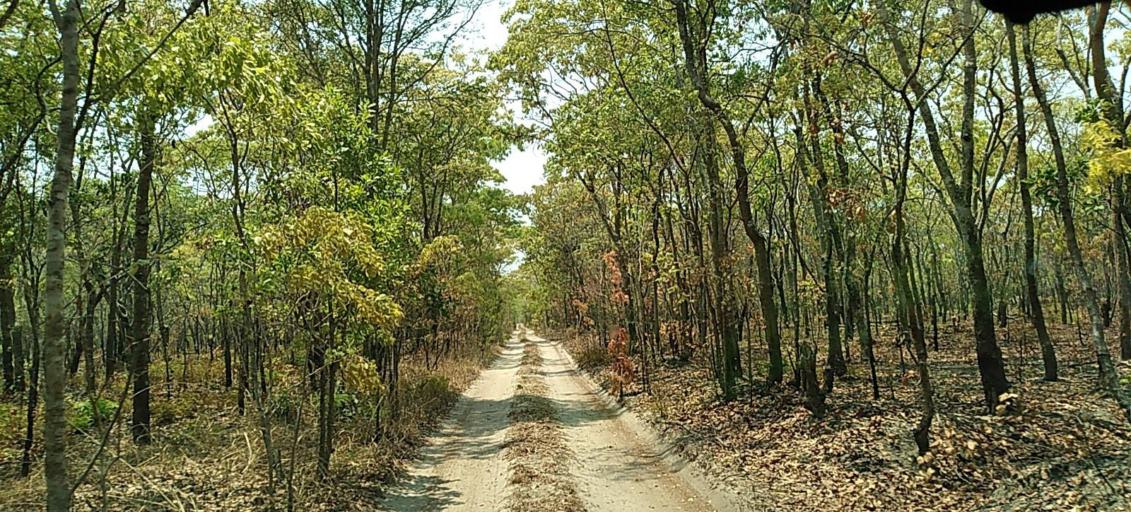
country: ZM
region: North-Western
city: Kabompo
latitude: -13.6534
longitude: 24.4692
